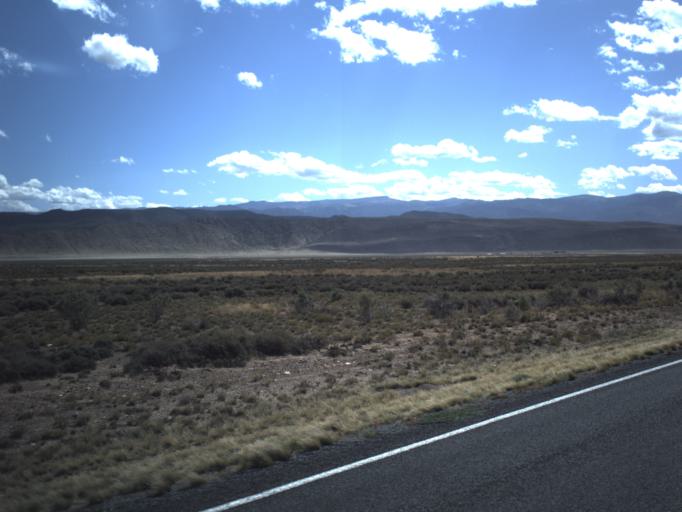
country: US
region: Utah
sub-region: Iron County
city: Enoch
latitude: 37.9144
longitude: -113.0315
